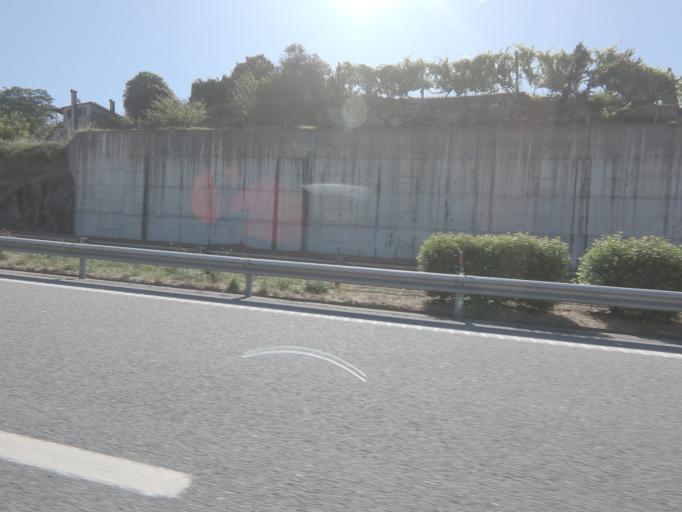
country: PT
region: Porto
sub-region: Marco de Canaveses
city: Marco de Canavezes
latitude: 41.2220
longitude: -8.1486
